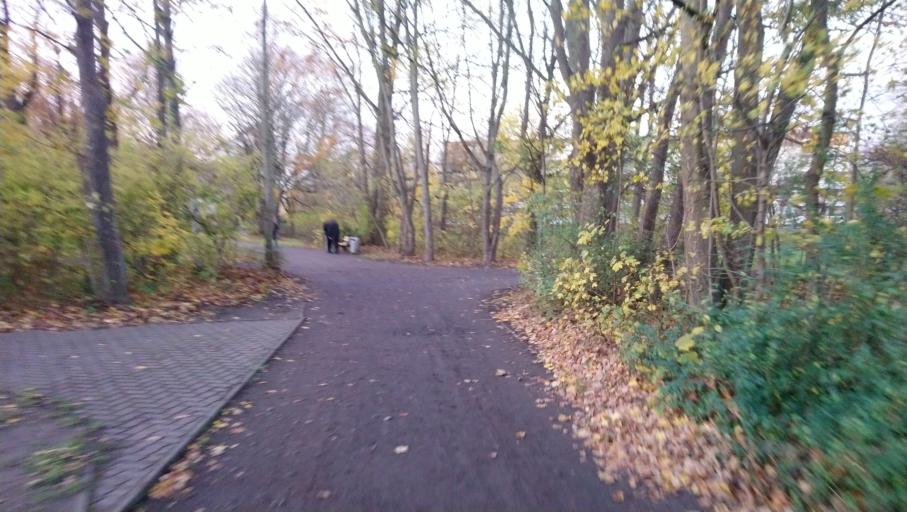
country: DE
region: Mecklenburg-Vorpommern
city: Rostock
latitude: 54.0678
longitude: 12.1191
